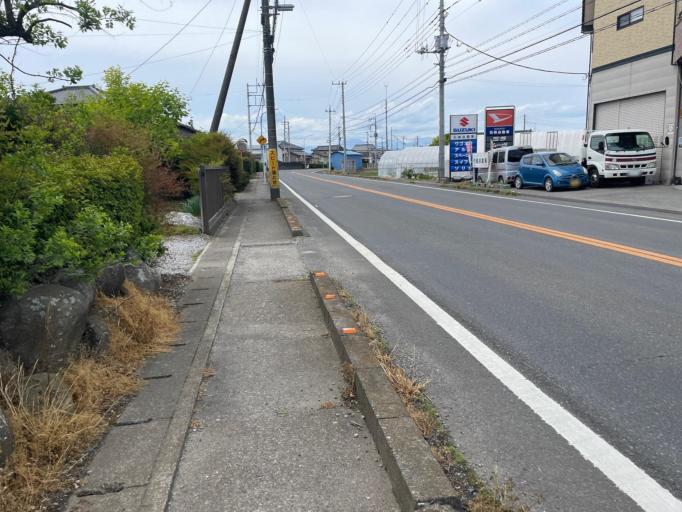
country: JP
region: Tochigi
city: Mibu
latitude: 36.4576
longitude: 139.7728
